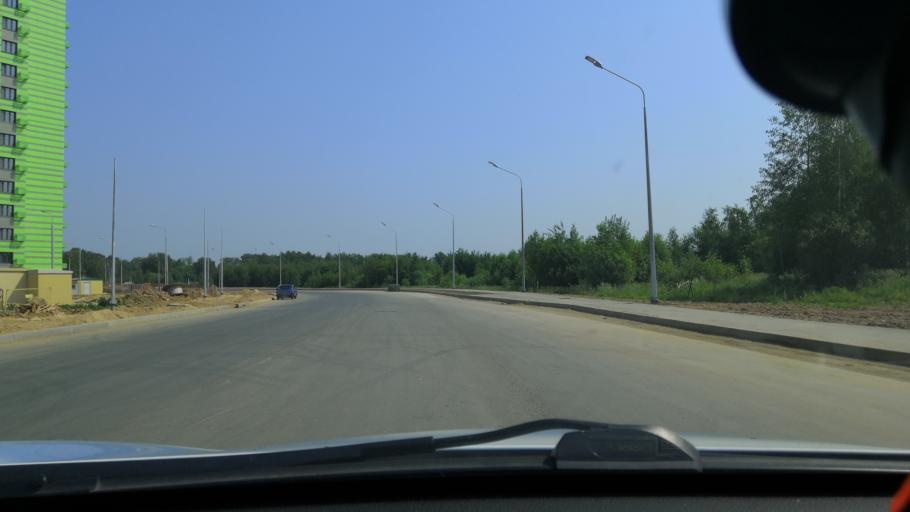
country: RU
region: Moscow
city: Severnyy
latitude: 55.9380
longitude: 37.5298
